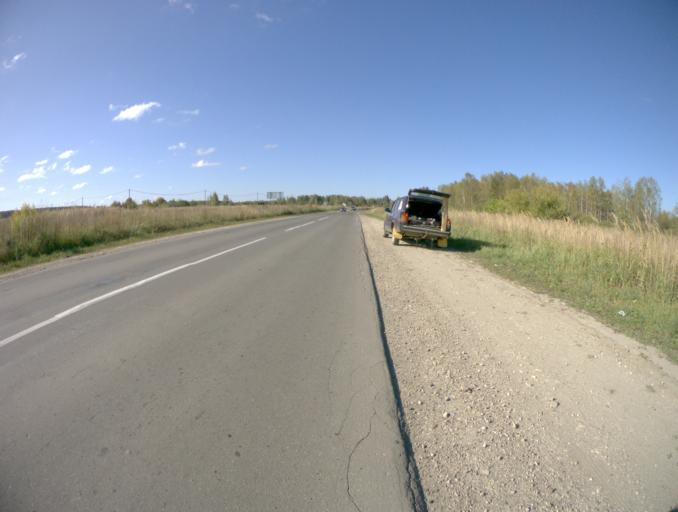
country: RU
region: Vladimir
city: Kameshkovo
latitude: 56.3449
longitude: 40.9615
